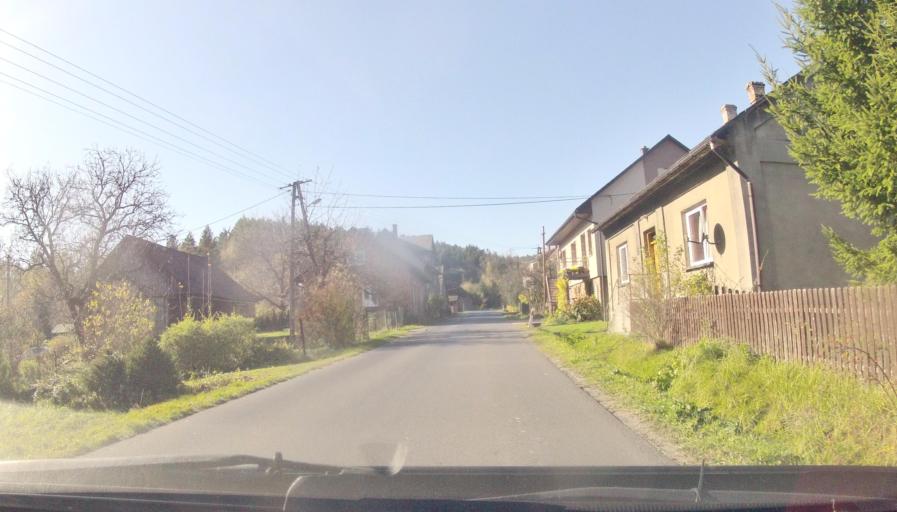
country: PL
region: Lesser Poland Voivodeship
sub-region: Powiat suski
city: Krzeszow
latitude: 49.7781
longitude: 19.4989
